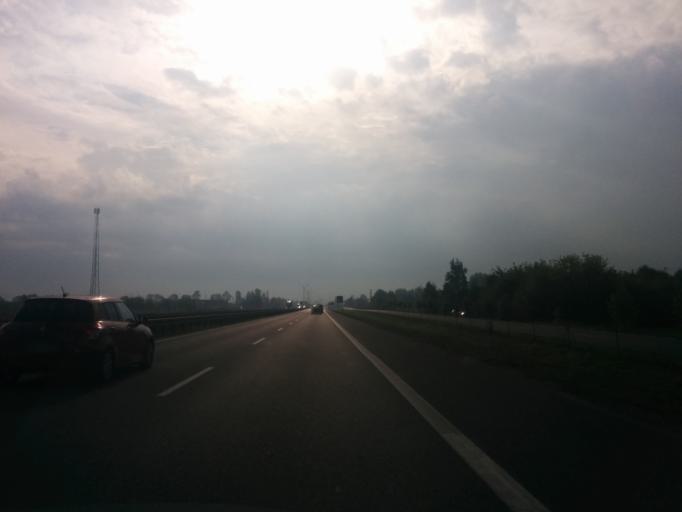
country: PL
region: Masovian Voivodeship
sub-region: Powiat radomski
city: Jedlinsk
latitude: 51.5253
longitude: 21.0946
